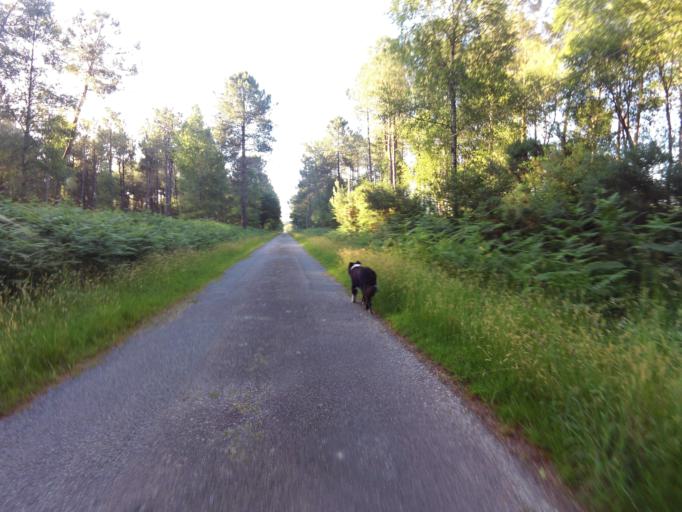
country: FR
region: Brittany
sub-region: Departement du Morbihan
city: Molac
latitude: 47.7413
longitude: -2.4208
